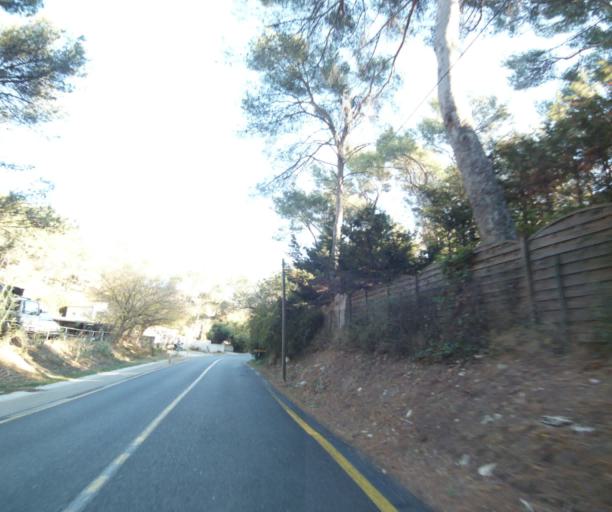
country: FR
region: Provence-Alpes-Cote d'Azur
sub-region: Departement des Bouches-du-Rhone
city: La Ciotat
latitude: 43.2001
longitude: 5.5887
